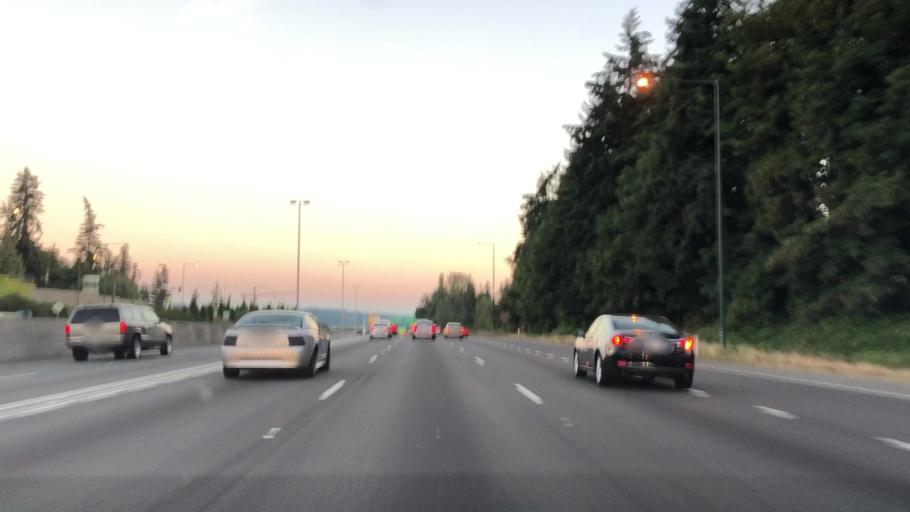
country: US
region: Washington
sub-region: King County
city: Bellevue
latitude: 47.6282
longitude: -122.1878
